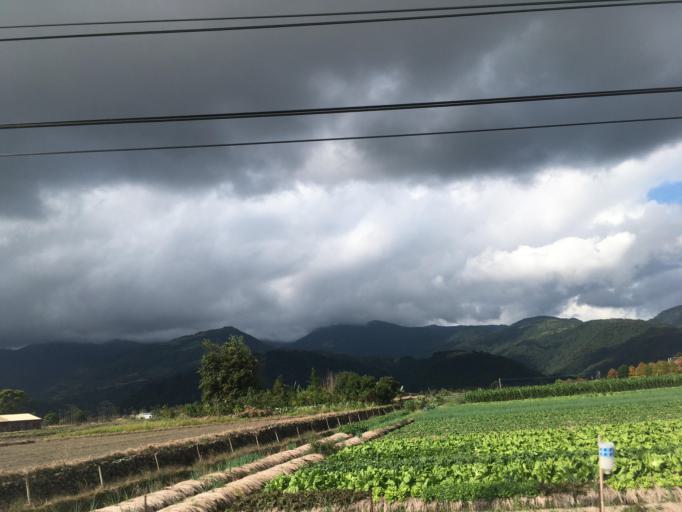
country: TW
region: Taiwan
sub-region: Yilan
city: Yilan
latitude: 24.6663
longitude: 121.6243
